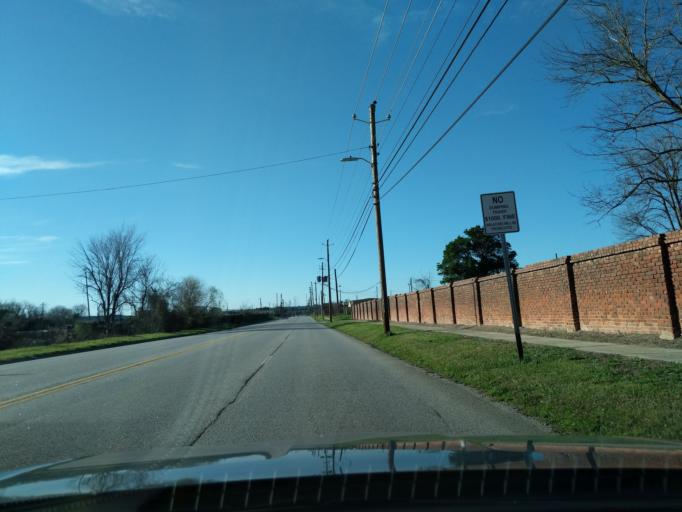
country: US
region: Georgia
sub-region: Richmond County
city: Augusta
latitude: 33.4585
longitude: -81.9592
